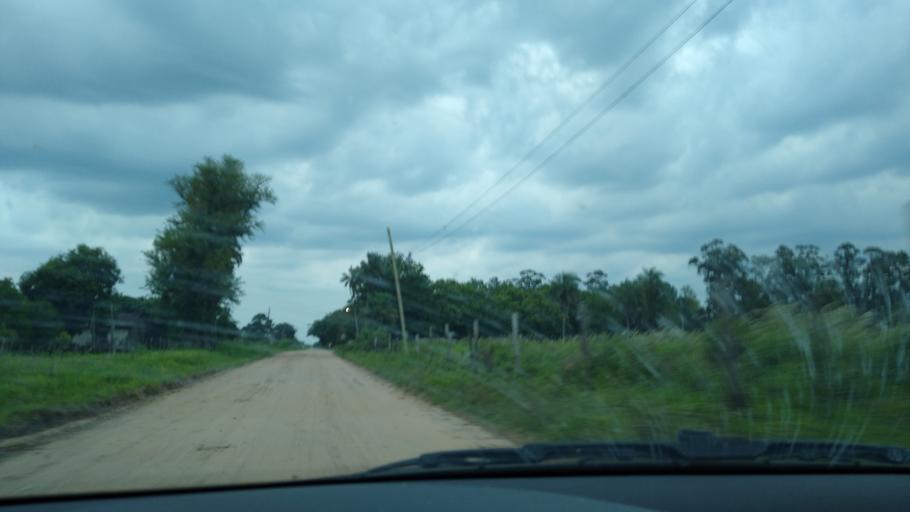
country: AR
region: Chaco
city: Puerto Vilelas
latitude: -27.5130
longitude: -58.9698
